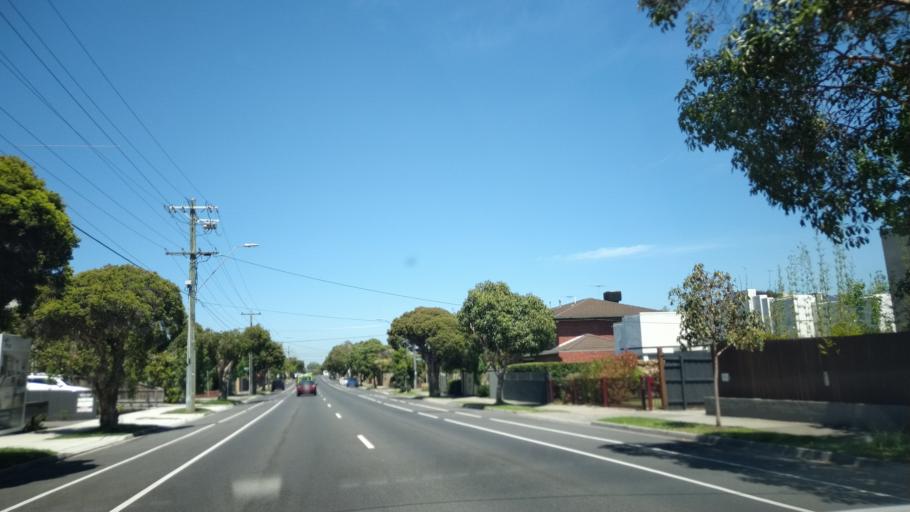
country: AU
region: Victoria
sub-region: Glen Eira
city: Caulfield South
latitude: -37.8972
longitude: 145.0270
